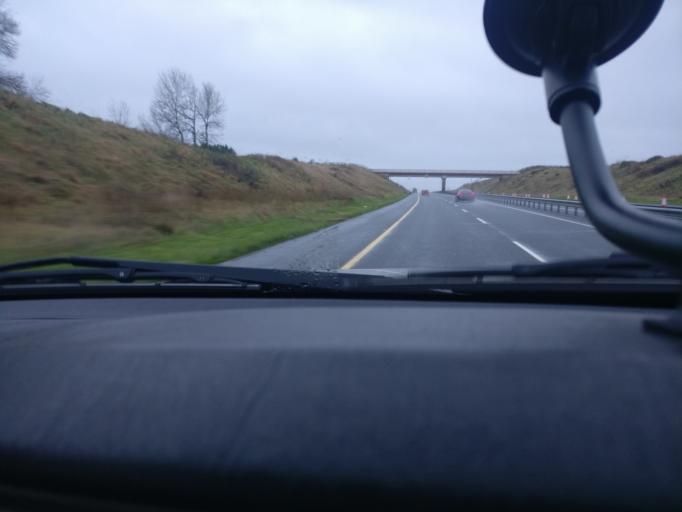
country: IE
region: Leinster
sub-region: An Iarmhi
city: Athlone
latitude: 53.3808
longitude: -8.0509
